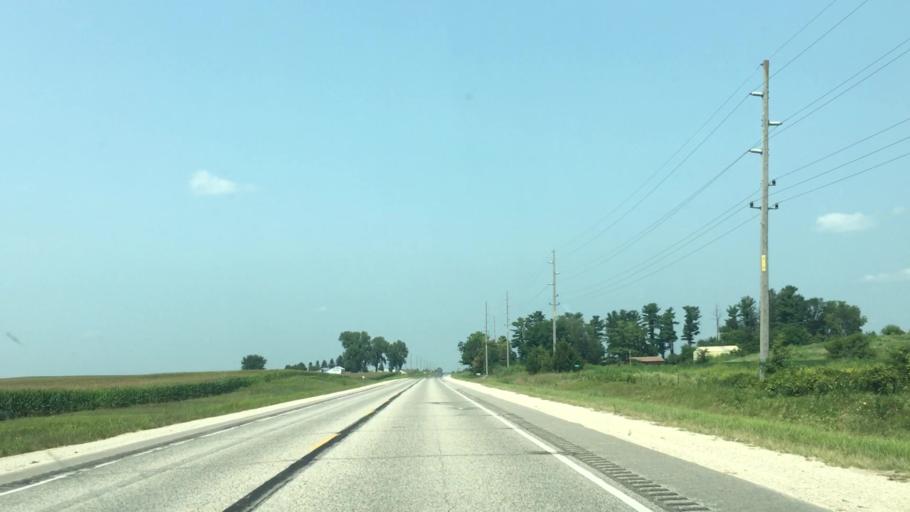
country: US
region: Iowa
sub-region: Fayette County
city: Fayette
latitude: 42.8778
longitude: -91.8105
